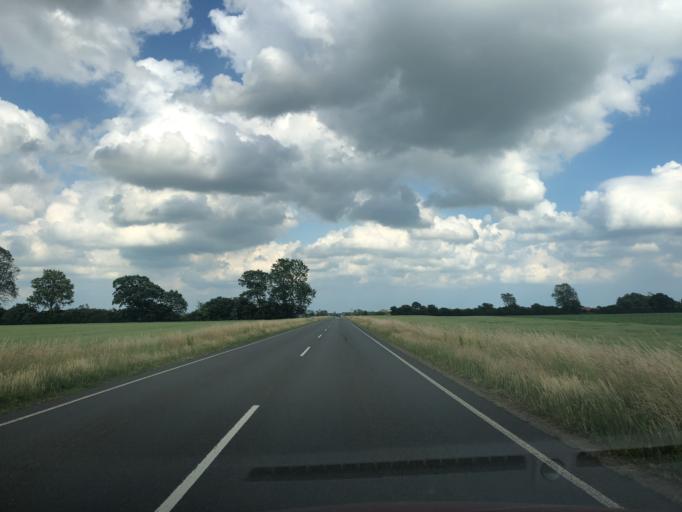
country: DK
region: Zealand
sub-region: Stevns Kommune
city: Harlev
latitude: 55.3163
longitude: 12.1906
